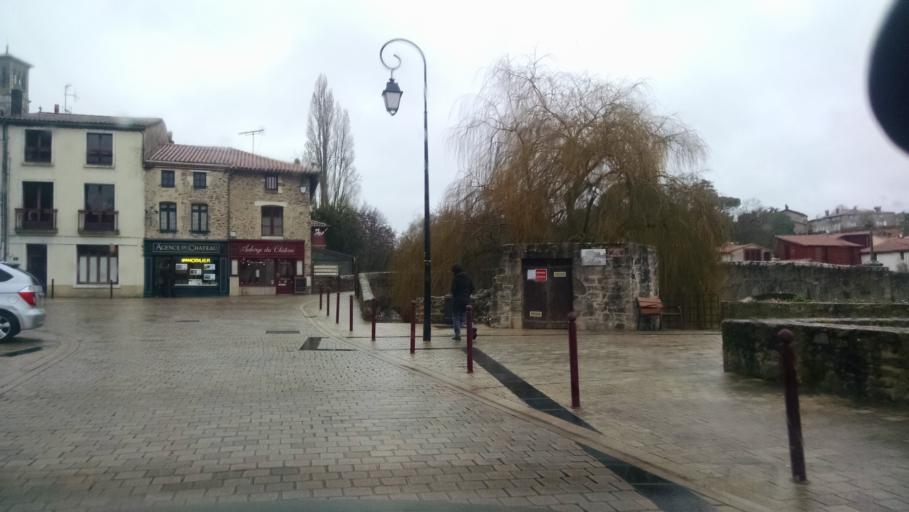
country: FR
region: Pays de la Loire
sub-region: Departement de la Loire-Atlantique
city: Clisson
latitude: 47.0866
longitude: -1.2798
